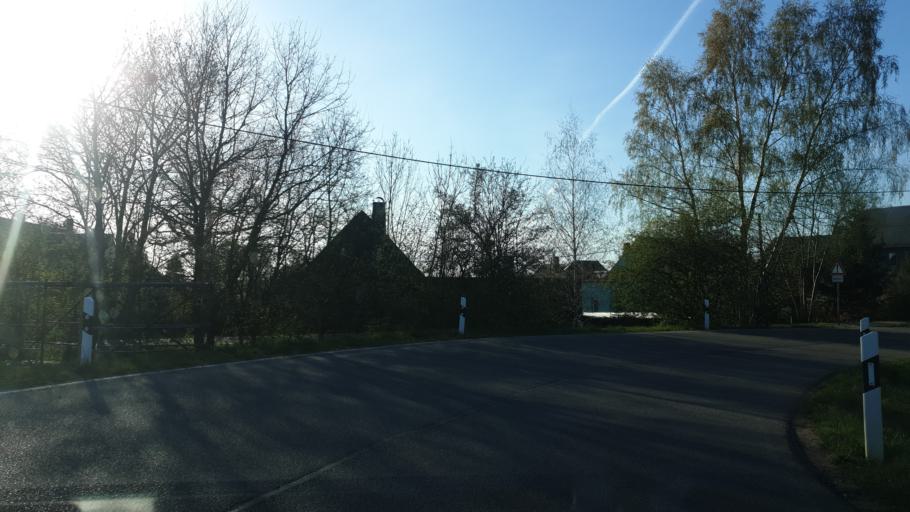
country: DE
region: Saxony
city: Niederdorf
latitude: 50.7605
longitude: 12.7725
